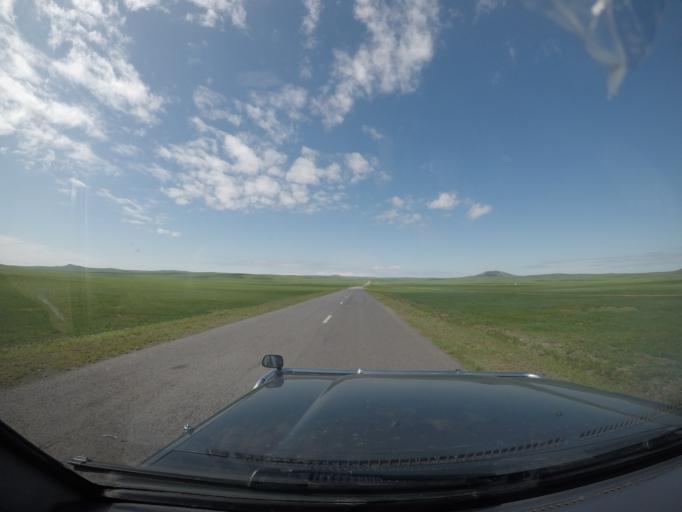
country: MN
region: Suhbaatar
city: Hanhohiy
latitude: 47.3723
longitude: 111.7739
